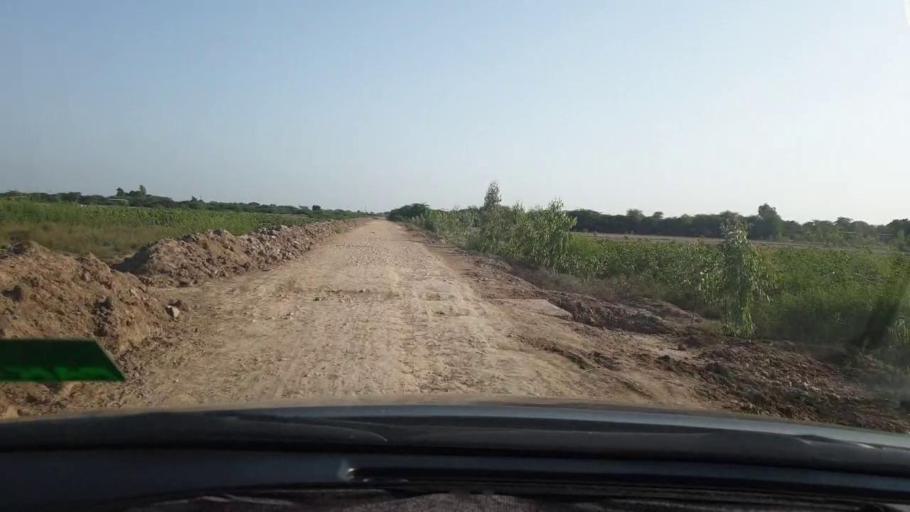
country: PK
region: Sindh
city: Naukot
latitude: 24.9076
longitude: 69.2765
